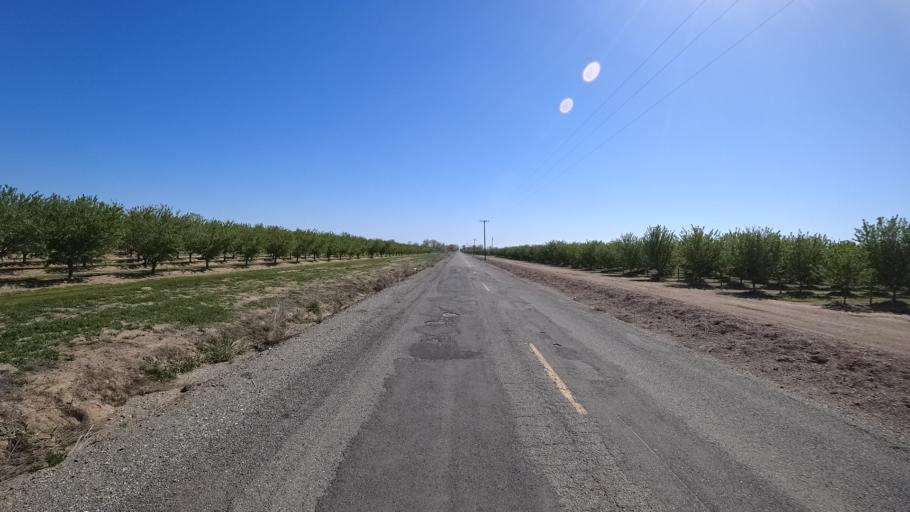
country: US
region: California
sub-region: Glenn County
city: Orland
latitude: 39.6972
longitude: -122.2362
